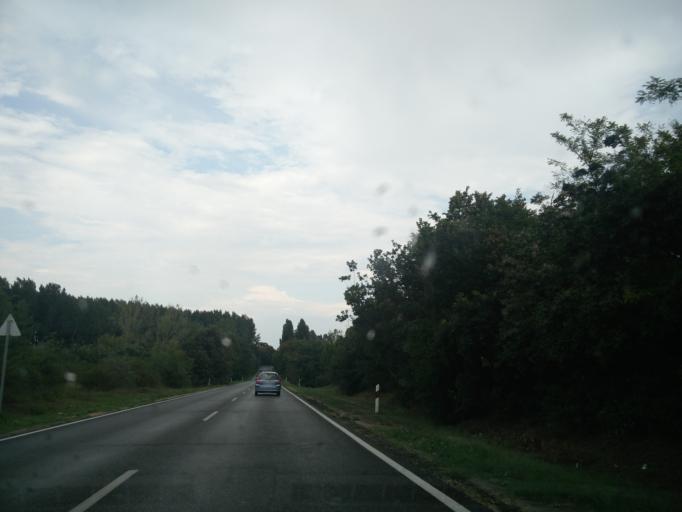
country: HU
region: Fejer
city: Szabadbattyan
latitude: 47.1053
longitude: 18.3547
